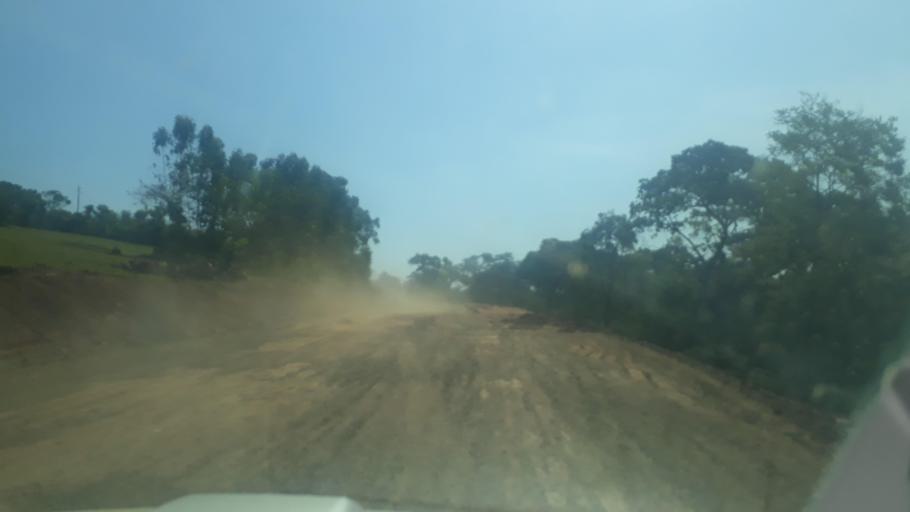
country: ET
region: Oromiya
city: Agaro
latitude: 7.7984
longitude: 36.7163
